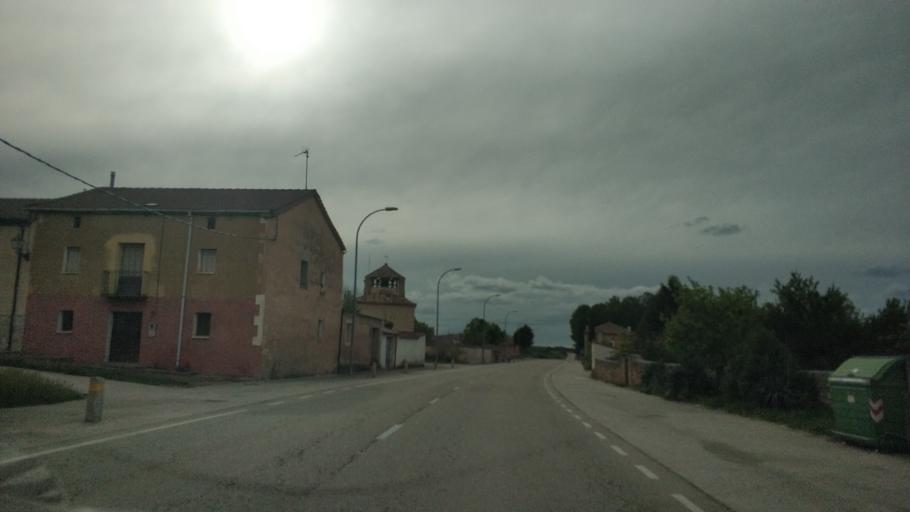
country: ES
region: Castille and Leon
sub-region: Provincia de Soria
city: Valdenebro
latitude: 41.5701
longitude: -3.0103
